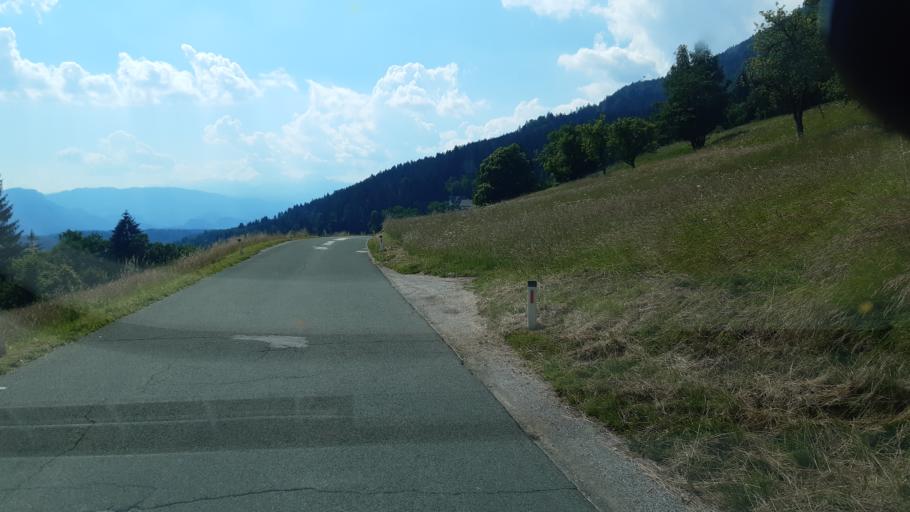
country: SI
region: Trzic
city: Bistrica pri Trzicu
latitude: 46.3586
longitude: 14.2670
